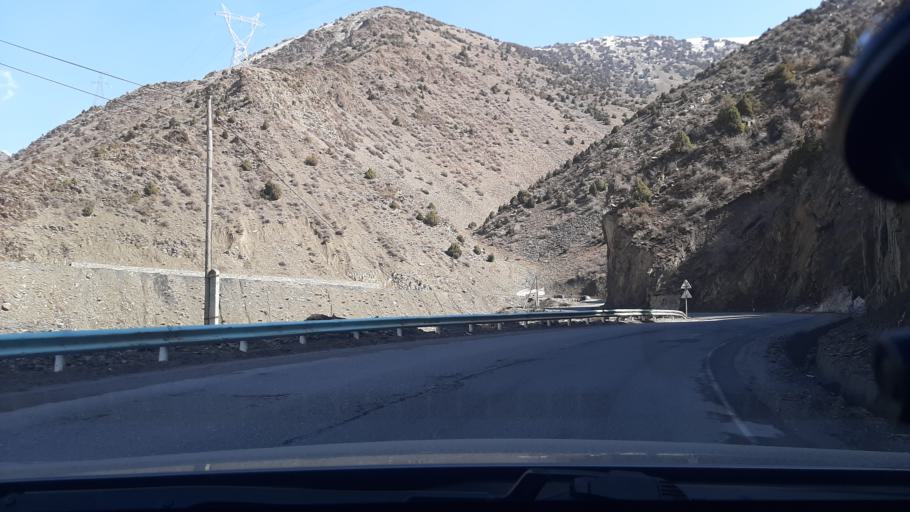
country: TJ
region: Viloyati Sughd
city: Ayni
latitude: 39.5039
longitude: 68.5517
